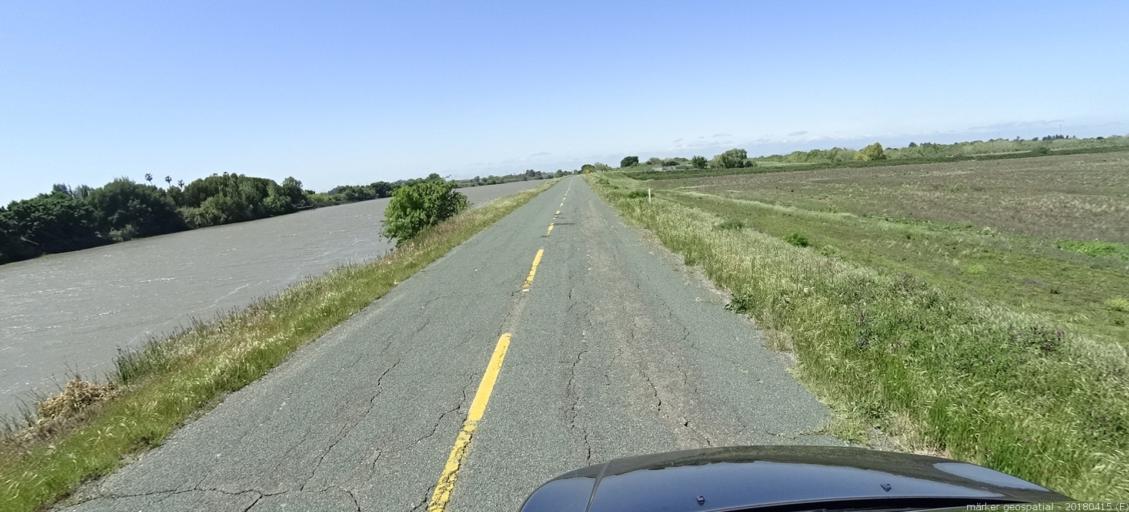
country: US
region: California
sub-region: Solano County
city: Rio Vista
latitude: 38.1735
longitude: -121.6430
